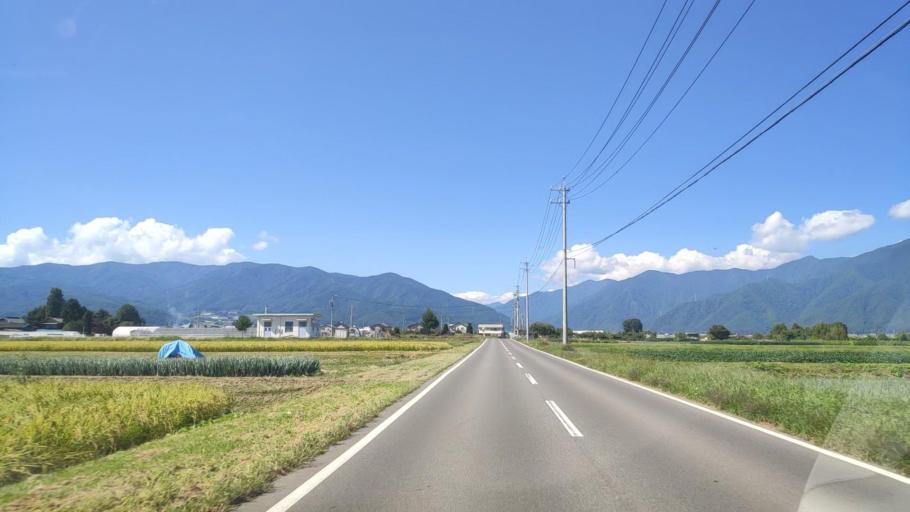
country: JP
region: Nagano
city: Matsumoto
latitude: 36.2003
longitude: 137.8936
